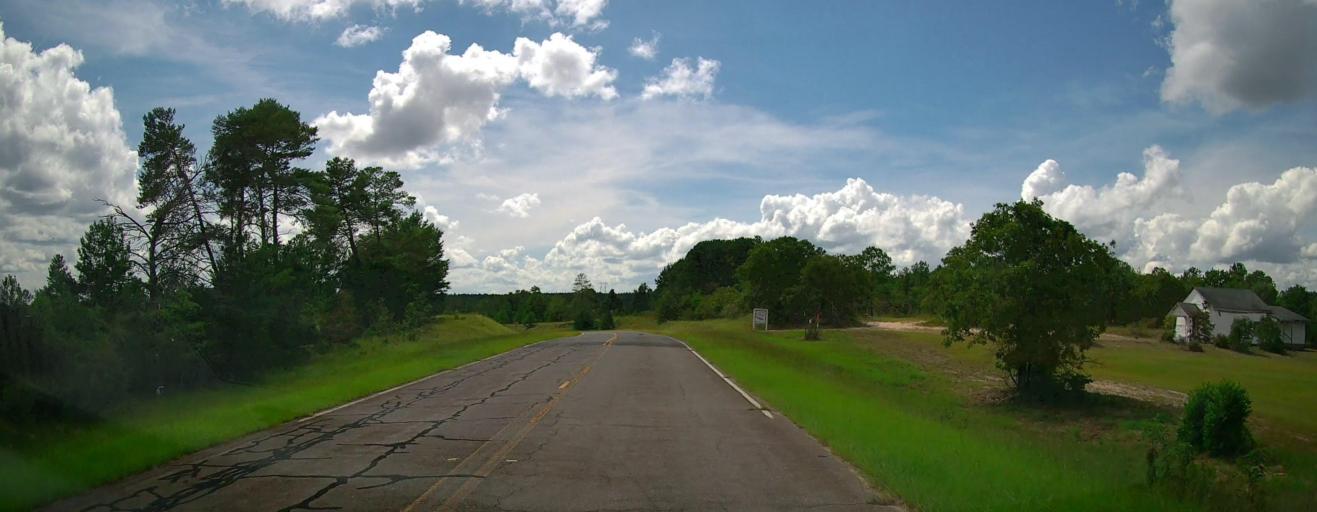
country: US
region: Georgia
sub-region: Taylor County
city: Butler
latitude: 32.5952
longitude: -84.3902
